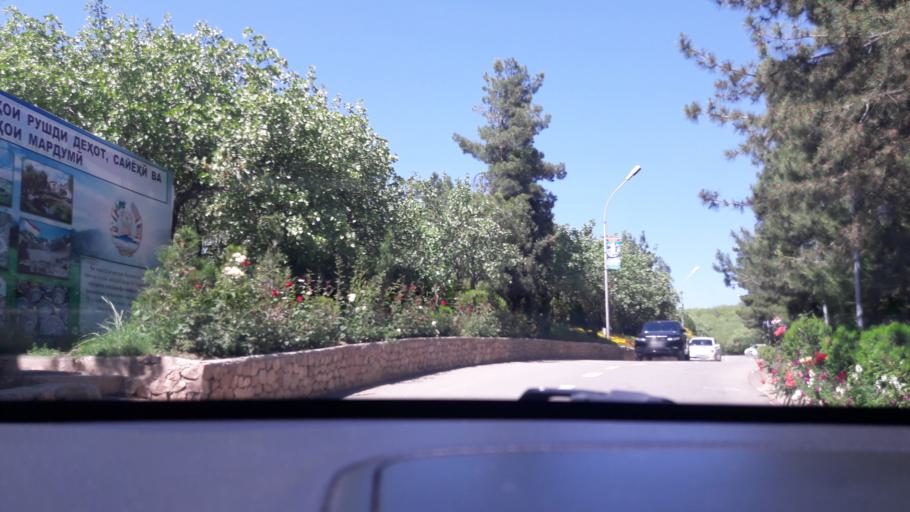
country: TJ
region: Dushanbe
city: Dushanbe
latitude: 38.5820
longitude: 68.8127
